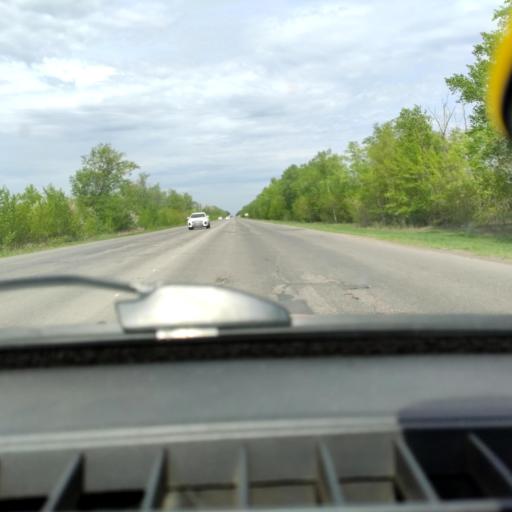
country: RU
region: Samara
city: Tol'yatti
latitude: 53.6067
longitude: 49.4108
